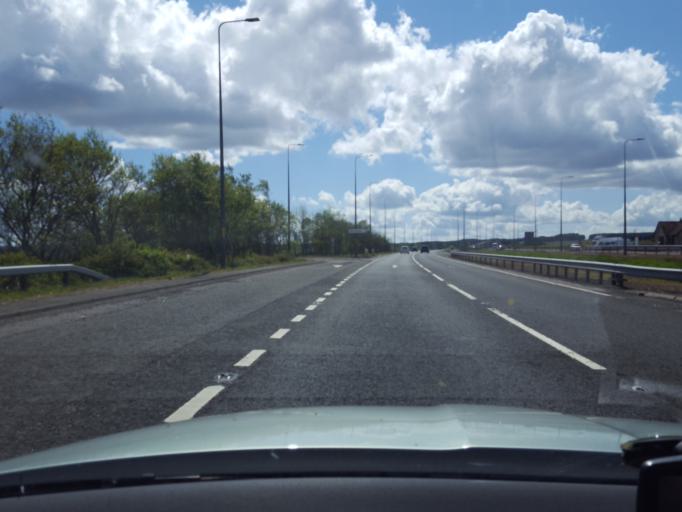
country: GB
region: Scotland
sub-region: Angus
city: Forfar
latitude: 56.5756
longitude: -2.9139
